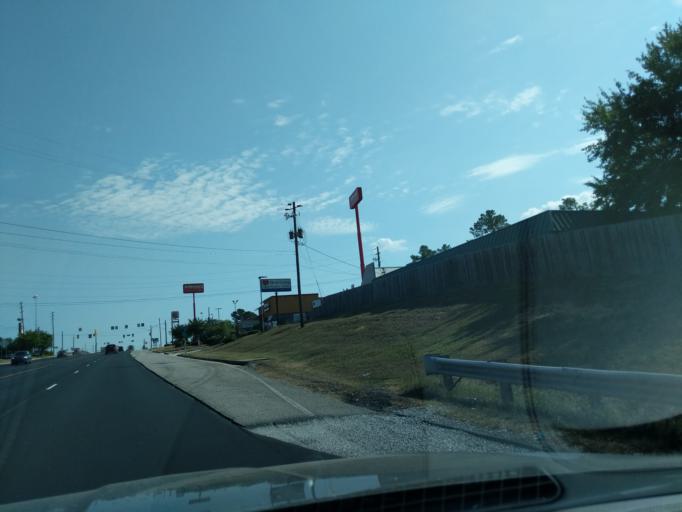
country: US
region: Georgia
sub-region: Columbia County
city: Evans
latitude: 33.4853
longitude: -82.1330
